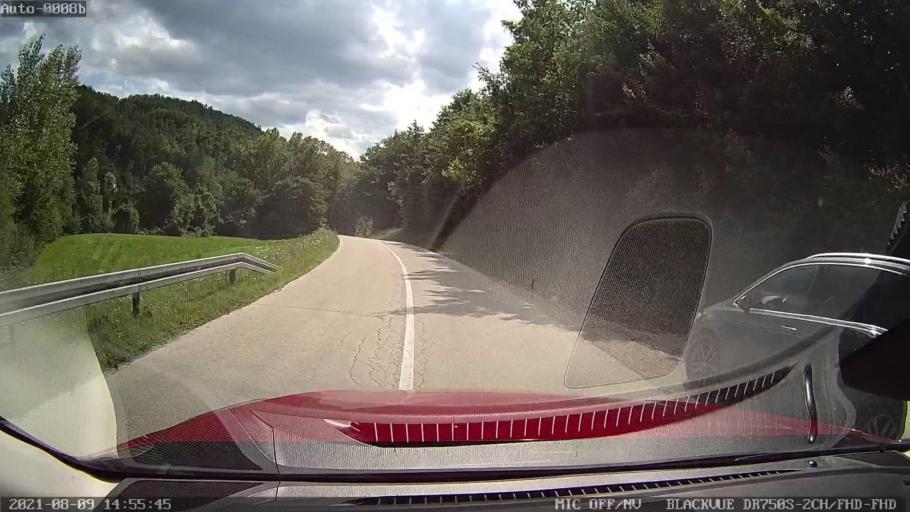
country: HR
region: Istarska
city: Pazin
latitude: 45.2741
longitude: 14.0633
